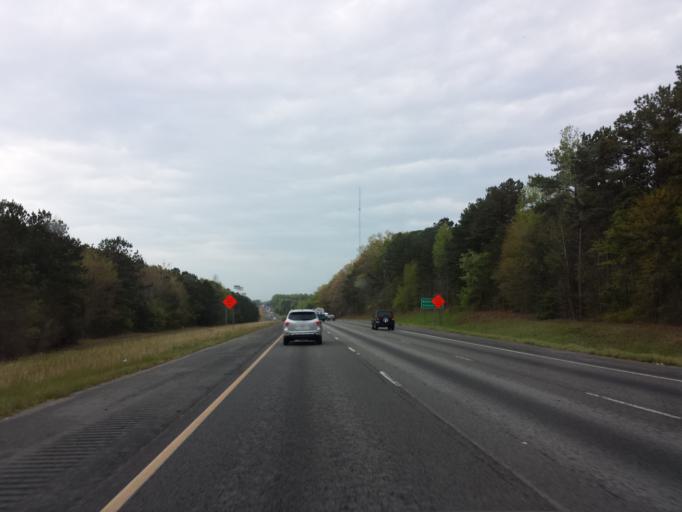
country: US
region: Georgia
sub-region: Henry County
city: Locust Grove
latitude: 33.3642
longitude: -84.1304
